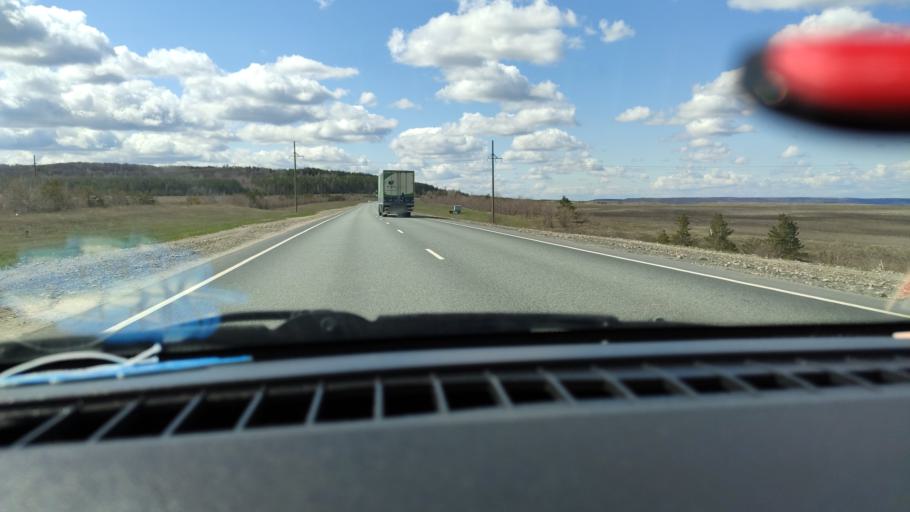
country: RU
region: Saratov
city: Khvalynsk
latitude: 52.5451
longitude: 48.0662
